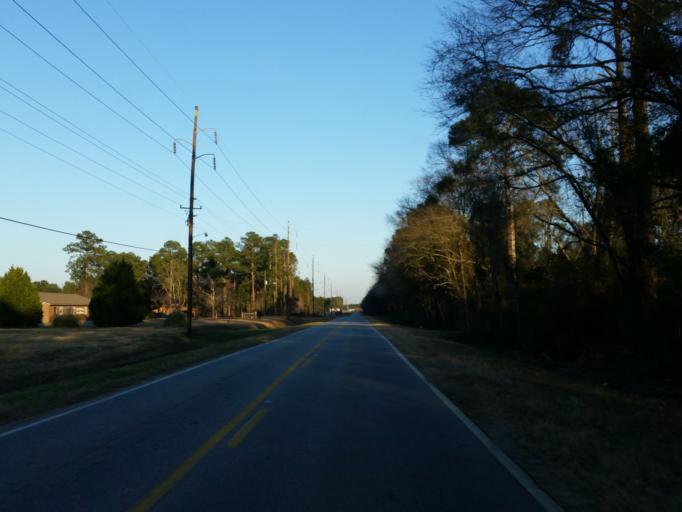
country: US
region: Georgia
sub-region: Crisp County
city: Cordele
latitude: 32.0041
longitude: -83.7762
